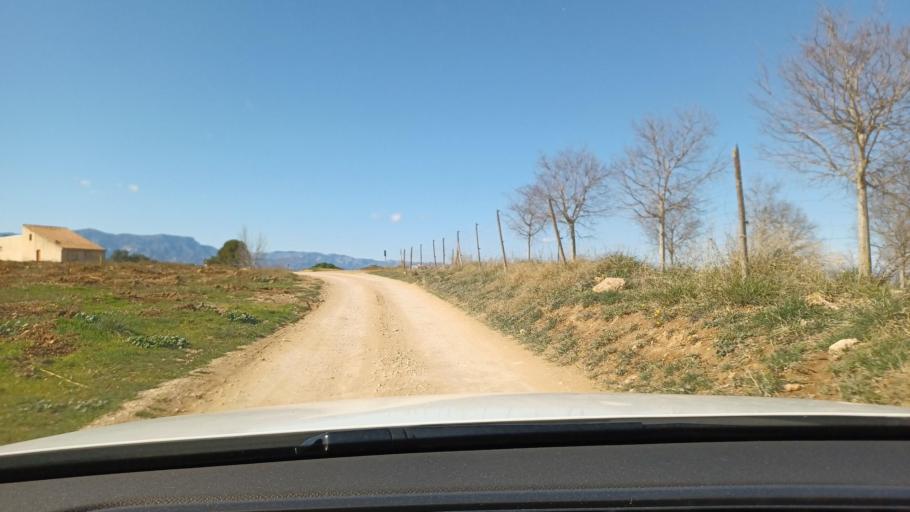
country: ES
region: Catalonia
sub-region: Provincia de Tarragona
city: Masdenverge
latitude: 40.6835
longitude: 0.5393
